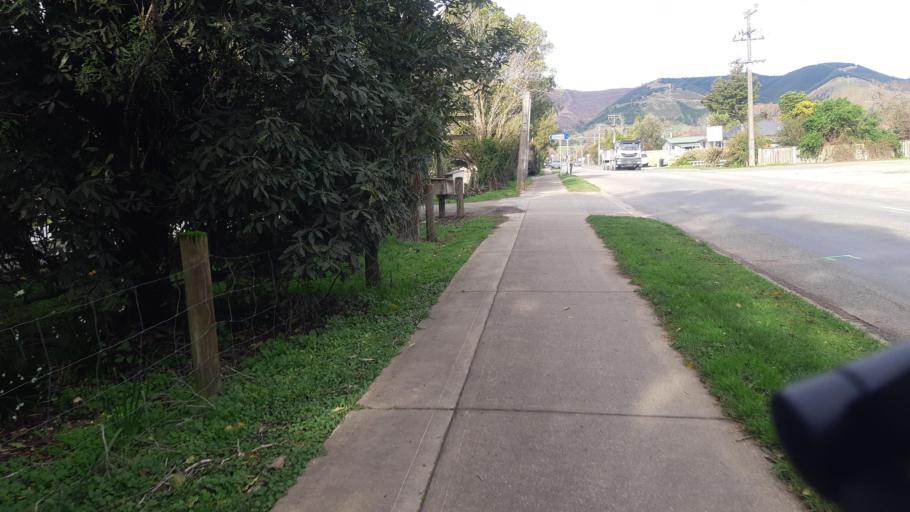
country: NZ
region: Tasman
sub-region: Tasman District
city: Richmond
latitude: -41.3524
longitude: 173.1519
